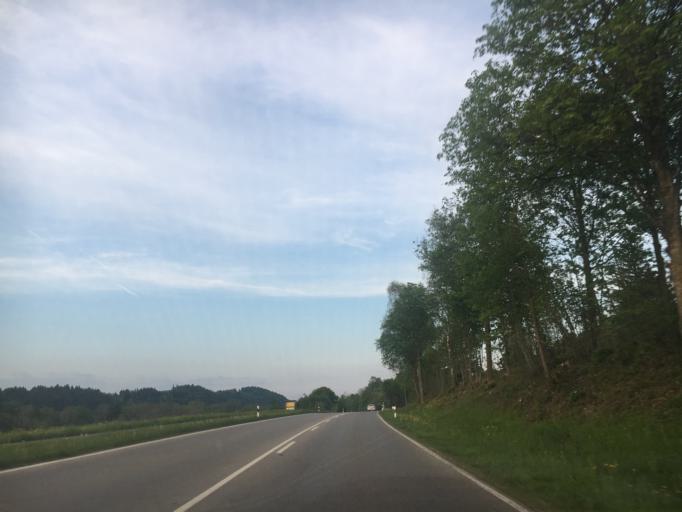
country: DE
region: Bavaria
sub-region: Upper Bavaria
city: Bad Heilbrunn
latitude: 47.7464
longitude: 11.4726
